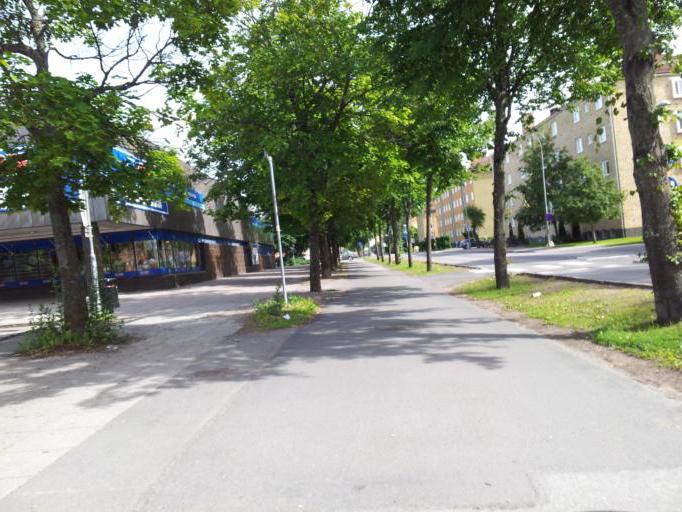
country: SE
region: Uppsala
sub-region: Uppsala Kommun
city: Uppsala
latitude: 59.8667
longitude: 17.6474
